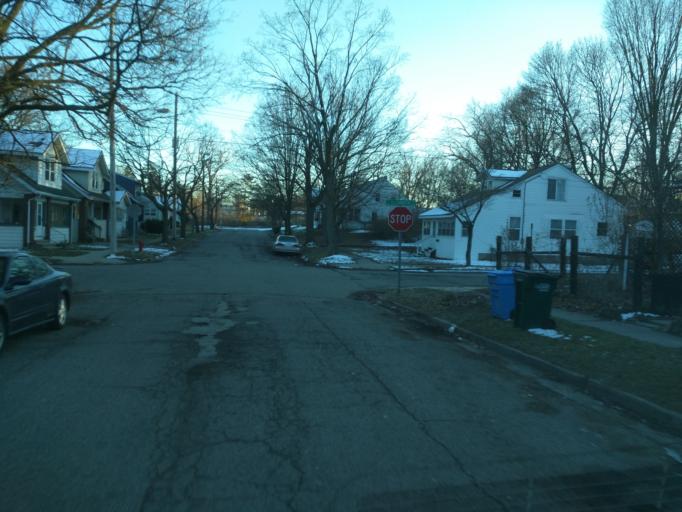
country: US
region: Michigan
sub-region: Ingham County
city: Lansing
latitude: 42.7276
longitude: -84.5285
